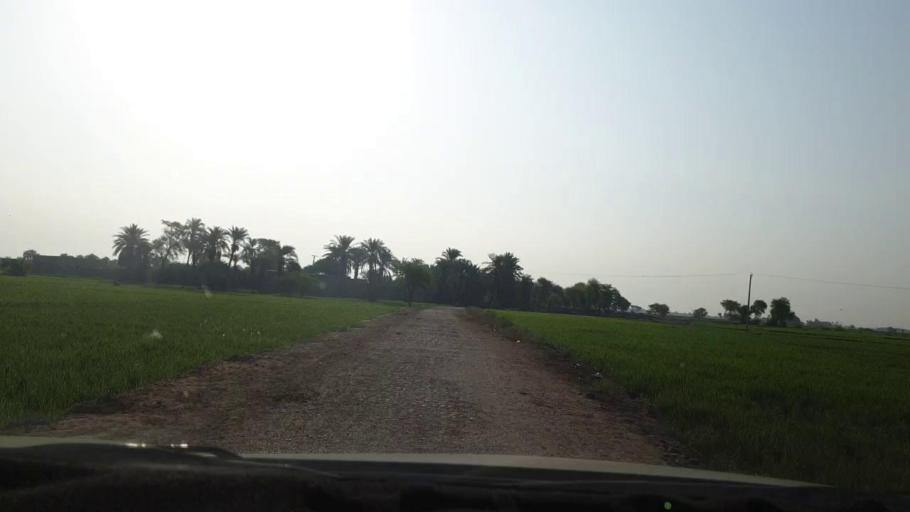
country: PK
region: Sindh
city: Larkana
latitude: 27.5118
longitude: 68.1804
